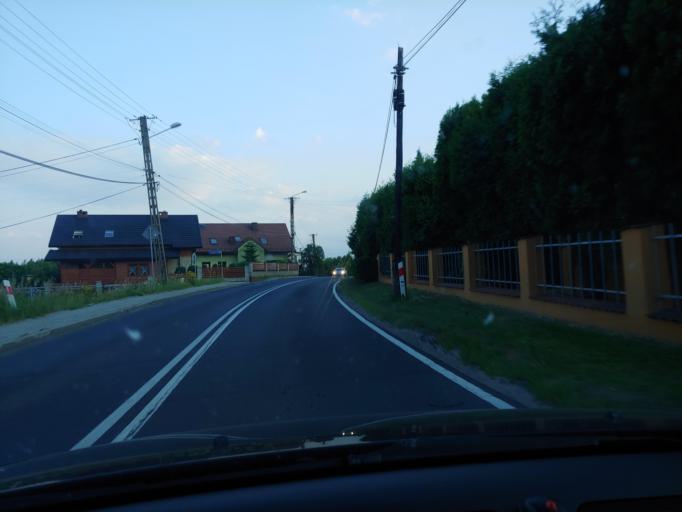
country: PL
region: Lesser Poland Voivodeship
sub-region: Powiat chrzanowski
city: Myslachowice
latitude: 50.1823
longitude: 19.4763
